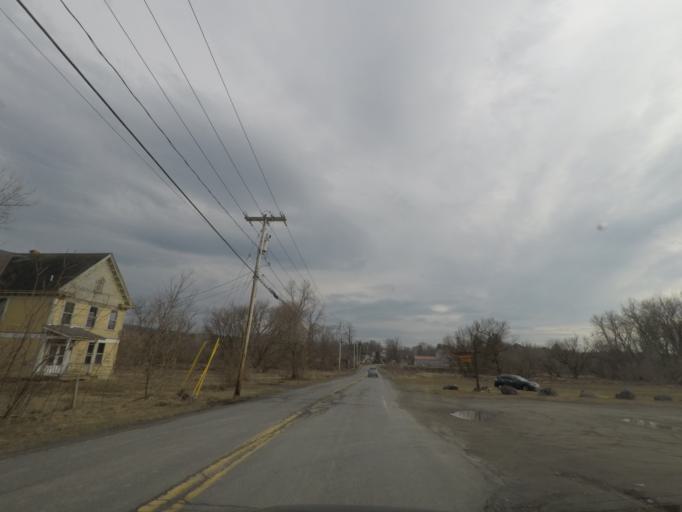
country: US
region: New York
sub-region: Washington County
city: Cambridge
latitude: 42.9579
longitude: -73.4330
